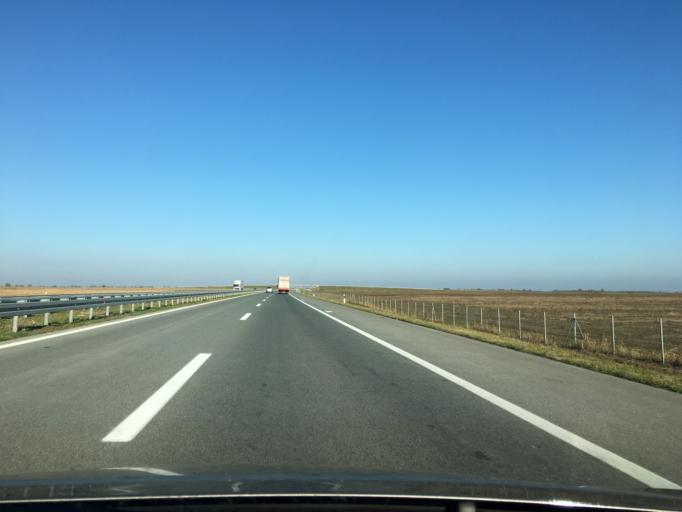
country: RS
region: Autonomna Pokrajina Vojvodina
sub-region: Severnobacki Okrug
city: Mali Igos
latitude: 45.7238
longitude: 19.7081
